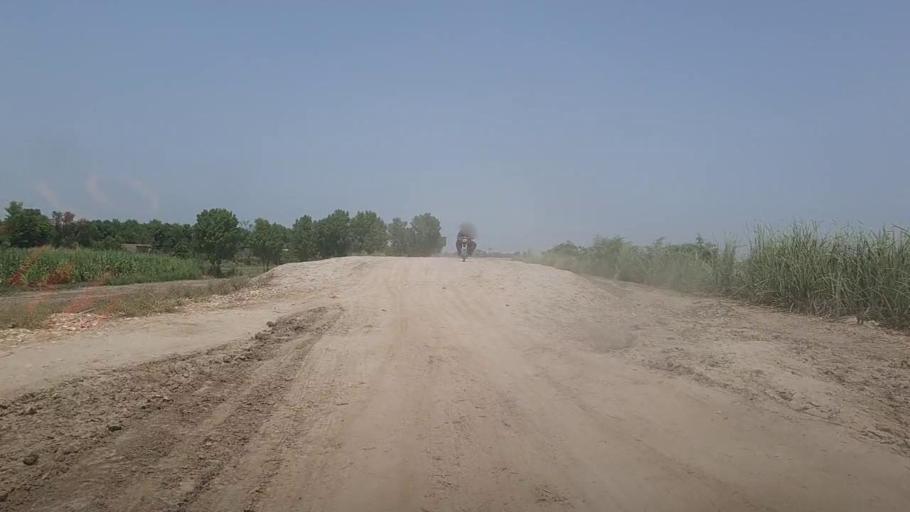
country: PK
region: Sindh
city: Pad Idan
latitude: 26.8052
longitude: 68.2719
